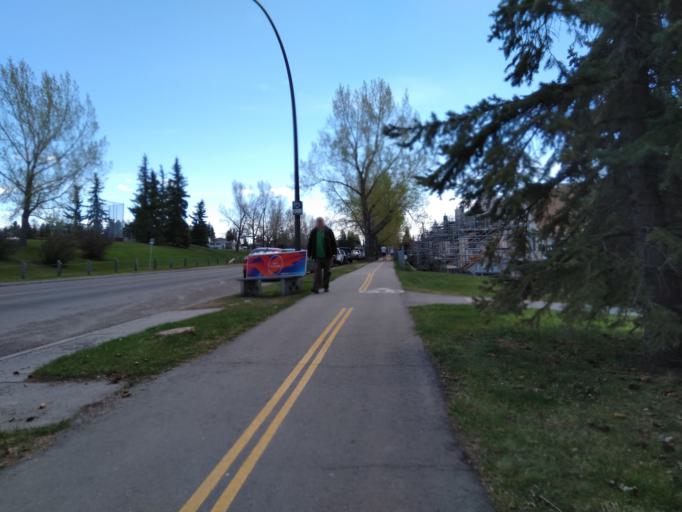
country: CA
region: Alberta
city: Calgary
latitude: 51.0151
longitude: -114.1599
